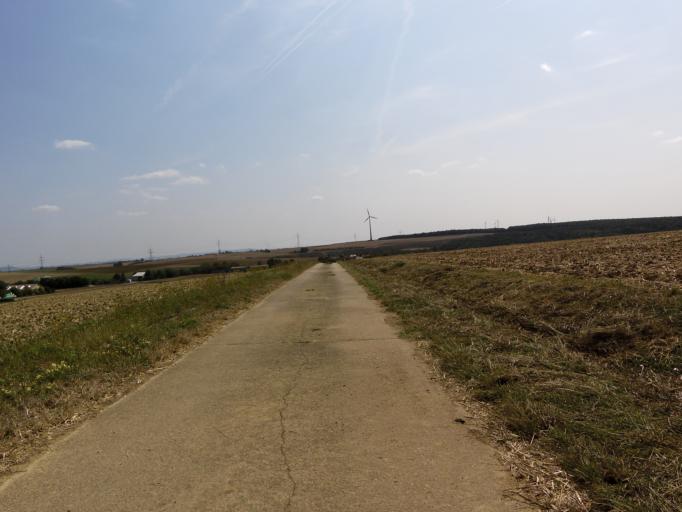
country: DE
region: Bavaria
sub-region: Regierungsbezirk Unterfranken
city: Theilheim
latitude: 49.7635
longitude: 10.0310
